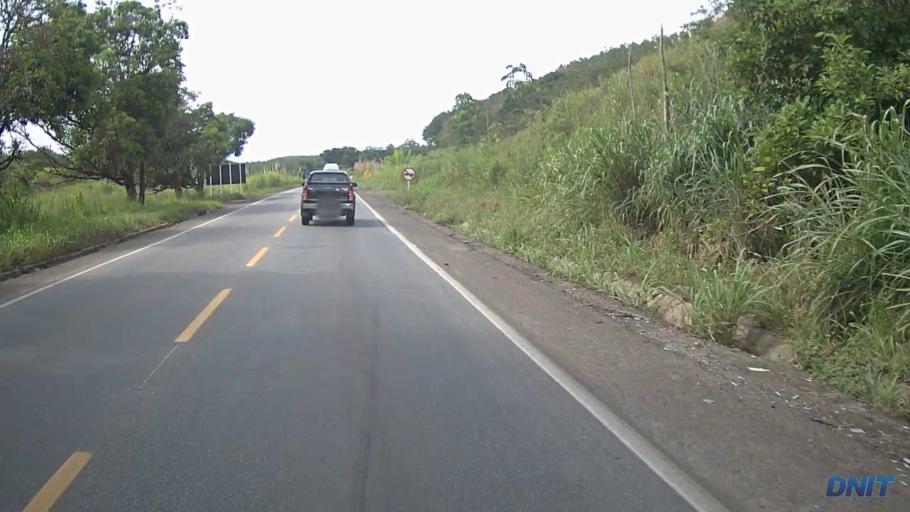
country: BR
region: Minas Gerais
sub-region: Ipaba
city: Ipaba
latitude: -19.3474
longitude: -42.4329
